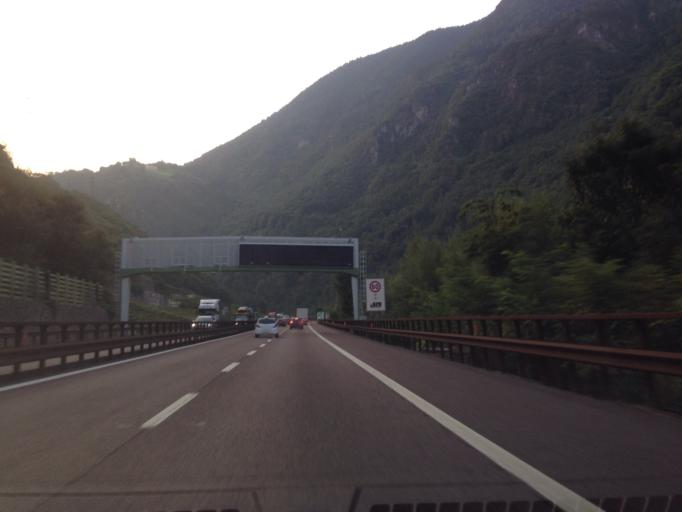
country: IT
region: Trentino-Alto Adige
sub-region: Bolzano
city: Cornedo All'Isarco
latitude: 46.4921
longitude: 11.4163
